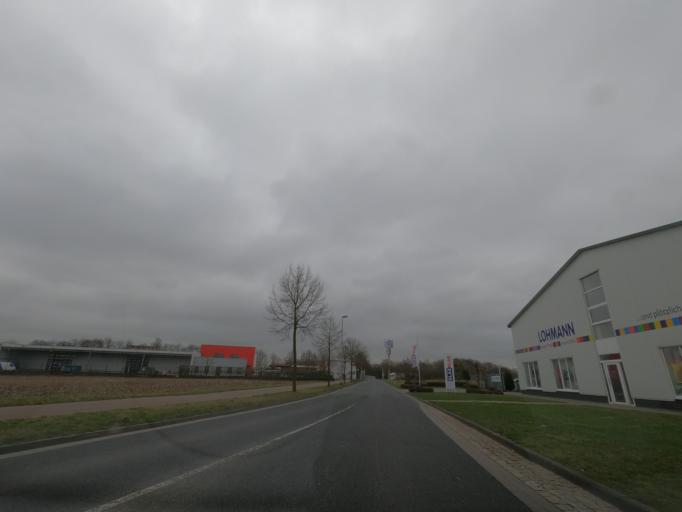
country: DE
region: Lower Saxony
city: Cloppenburg
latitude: 52.8290
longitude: 7.9991
